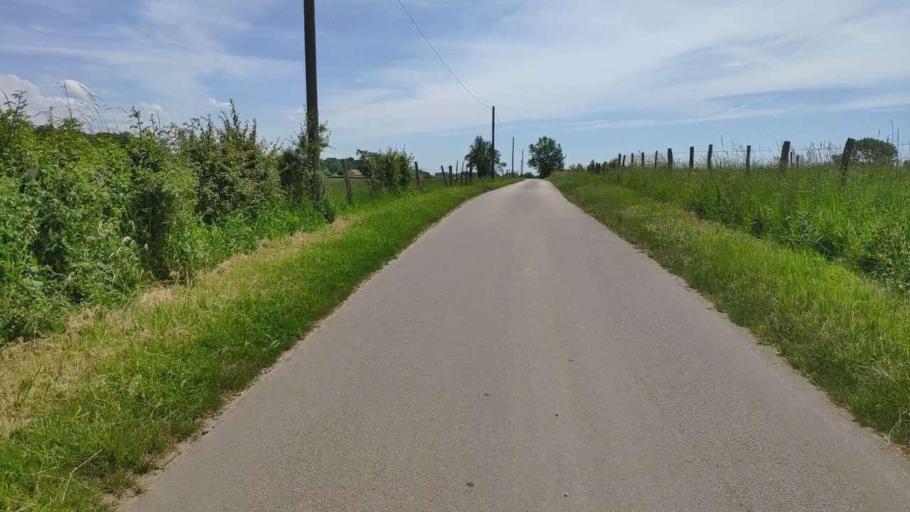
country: FR
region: Franche-Comte
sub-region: Departement du Jura
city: Bletterans
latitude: 46.7708
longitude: 5.4321
